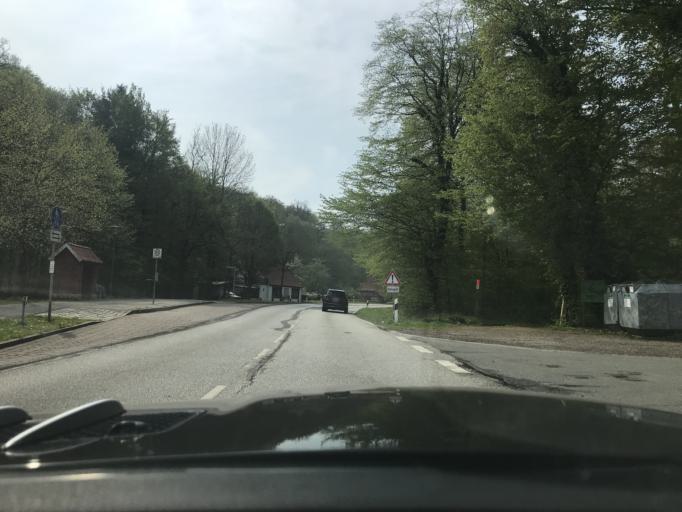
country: DE
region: Schleswig-Holstein
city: Gromitz
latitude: 54.1861
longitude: 10.9812
